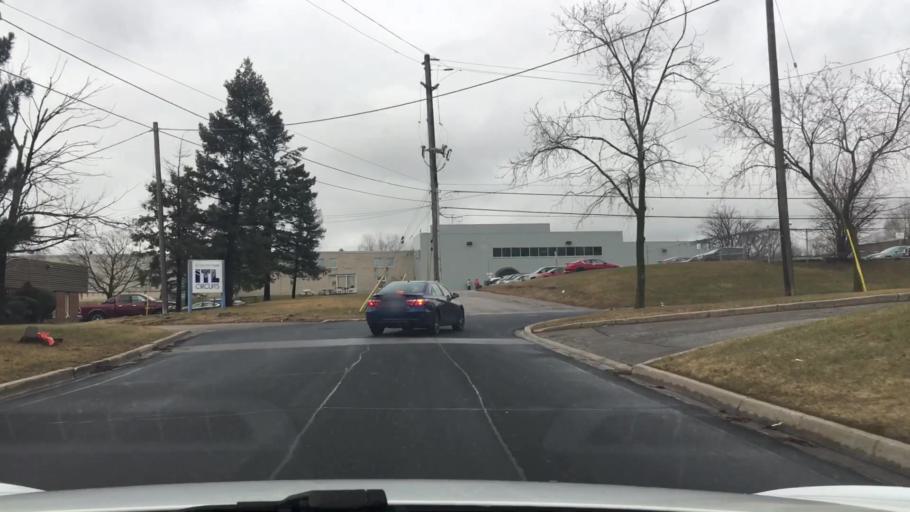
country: CA
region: Ontario
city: Willowdale
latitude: 43.8239
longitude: -79.3489
